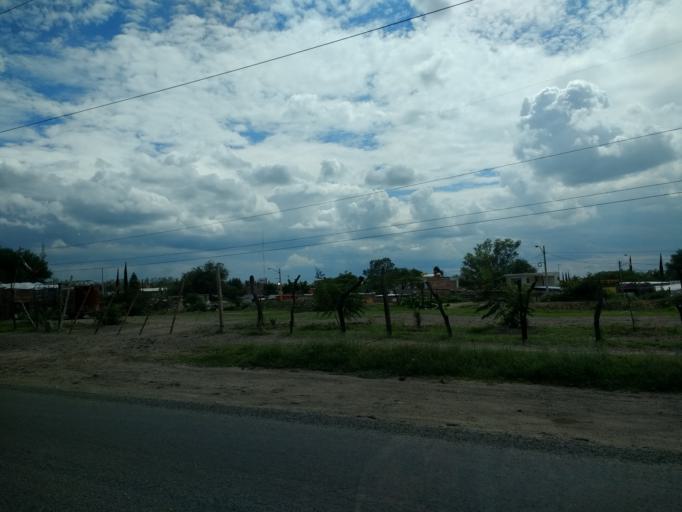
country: MX
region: Aguascalientes
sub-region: Aguascalientes
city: Aguascalientes
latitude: 21.8851
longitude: -102.2602
